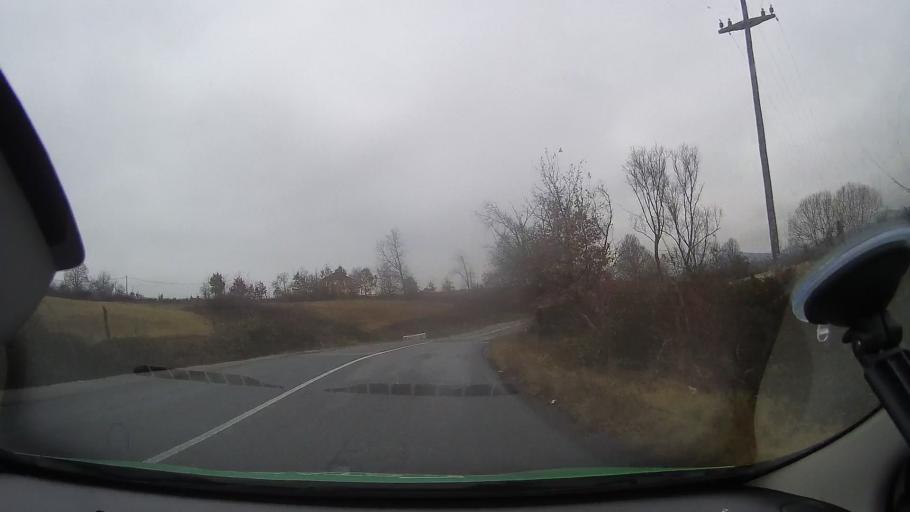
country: RO
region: Arad
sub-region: Comuna Varfurile
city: Varfurile
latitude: 46.3247
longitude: 22.4954
